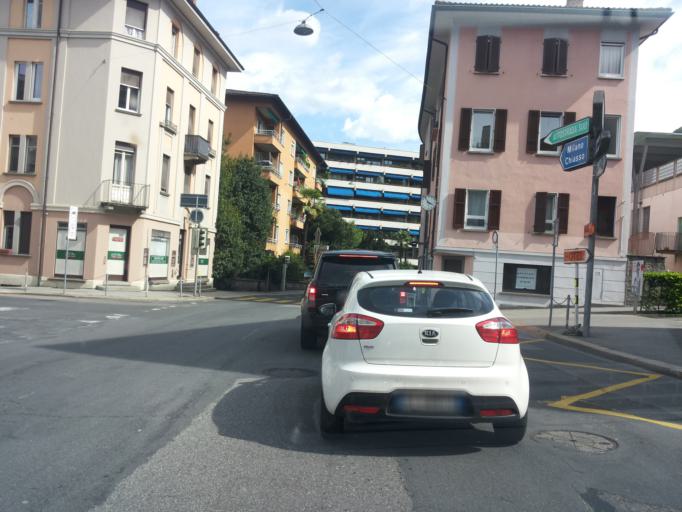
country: CH
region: Ticino
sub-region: Lugano District
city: Sorengo
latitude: 45.9973
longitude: 8.9432
